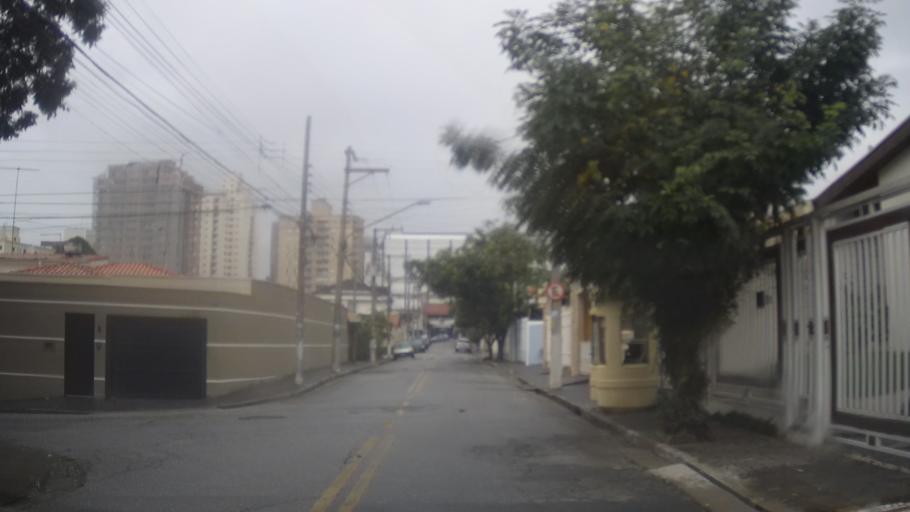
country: BR
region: Sao Paulo
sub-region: Guarulhos
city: Guarulhos
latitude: -23.4595
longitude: -46.5308
